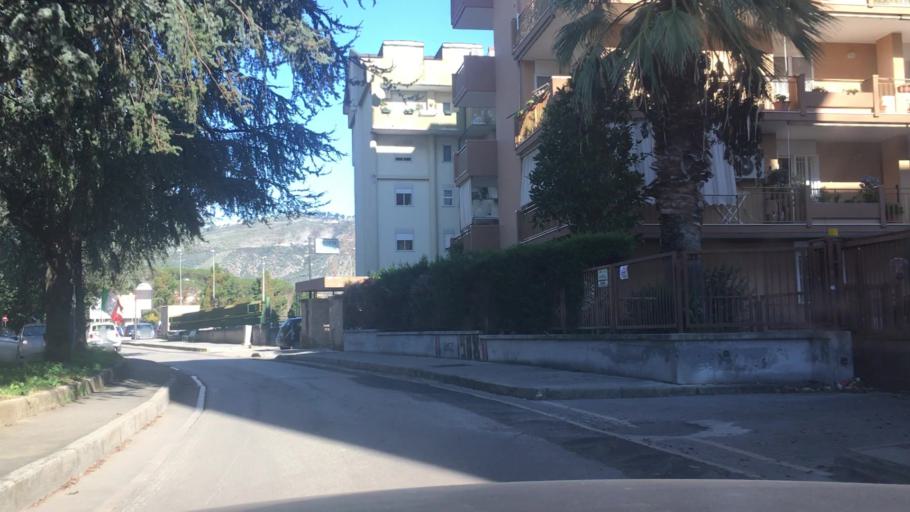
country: IT
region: Campania
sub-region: Provincia di Caserta
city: Caserta
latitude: 41.0704
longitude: 14.3535
